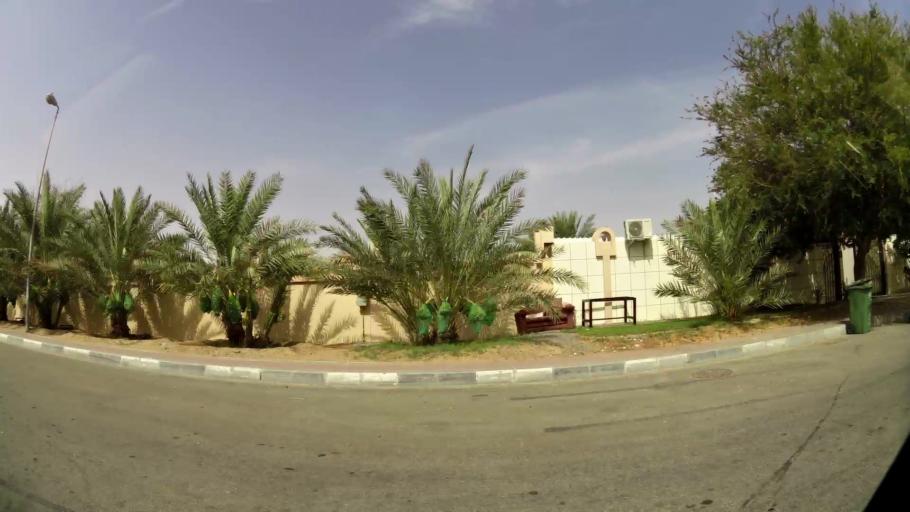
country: AE
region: Abu Dhabi
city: Al Ain
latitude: 24.1612
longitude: 55.6838
